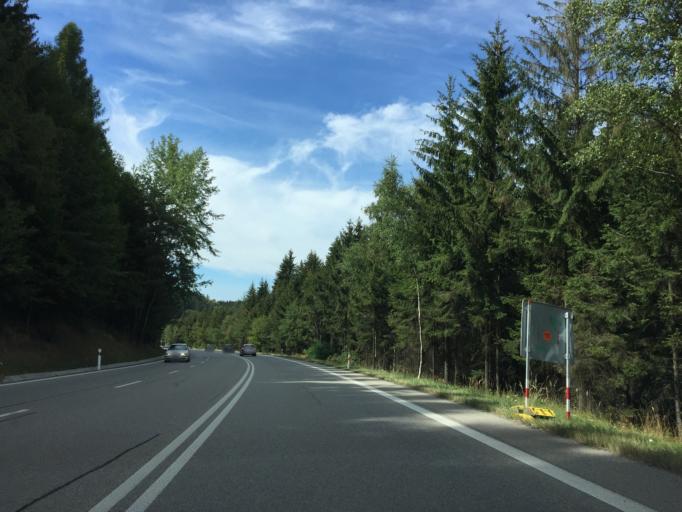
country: CZ
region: Central Bohemia
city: Votice
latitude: 49.6210
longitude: 14.6572
